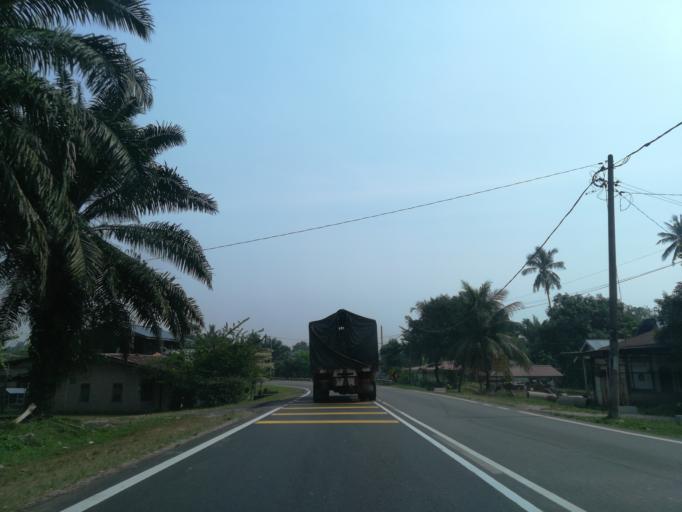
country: MY
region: Penang
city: Tasek Glugor
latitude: 5.4611
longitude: 100.5470
